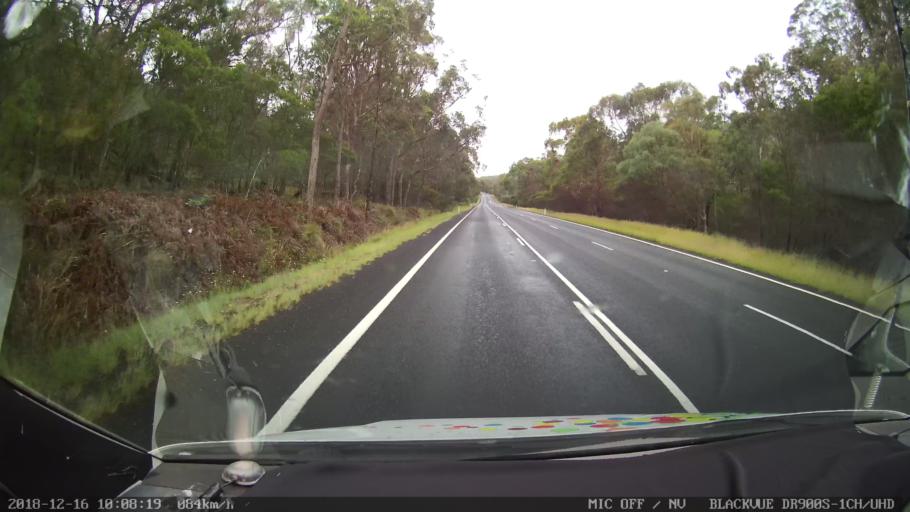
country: AU
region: New South Wales
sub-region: Glen Innes Severn
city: Glen Innes
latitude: -29.3300
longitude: 151.9052
